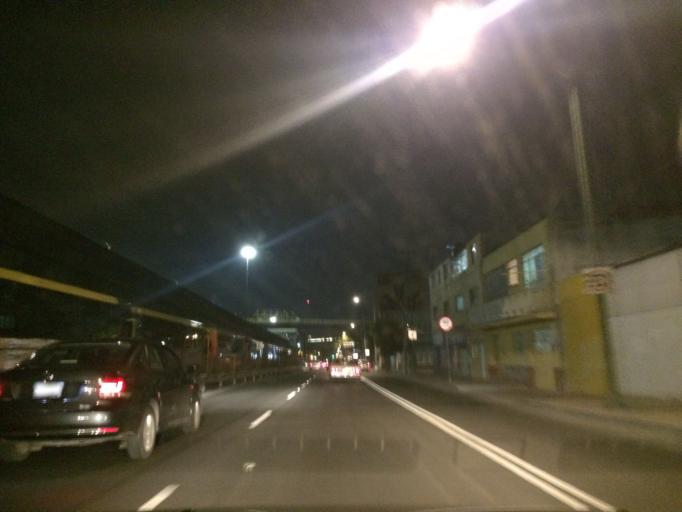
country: MX
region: Mexico City
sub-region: Iztacalco
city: Iztacalco
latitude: 19.4082
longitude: -99.0882
